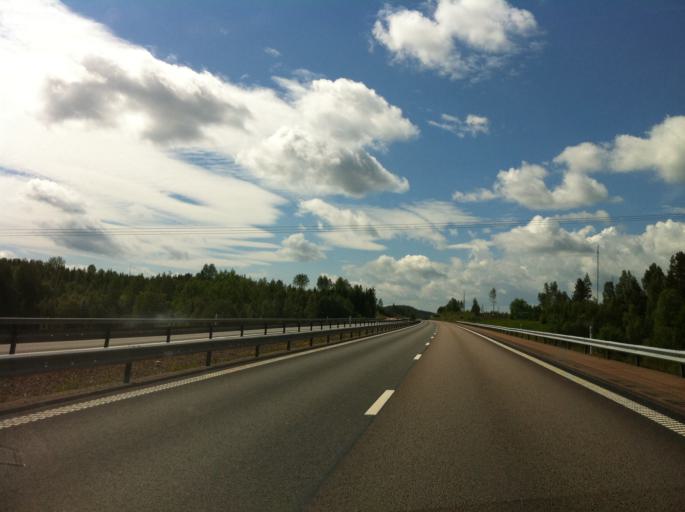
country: SE
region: Vaermland
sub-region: Grums Kommun
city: Slottsbron
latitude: 59.2709
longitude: 13.0109
